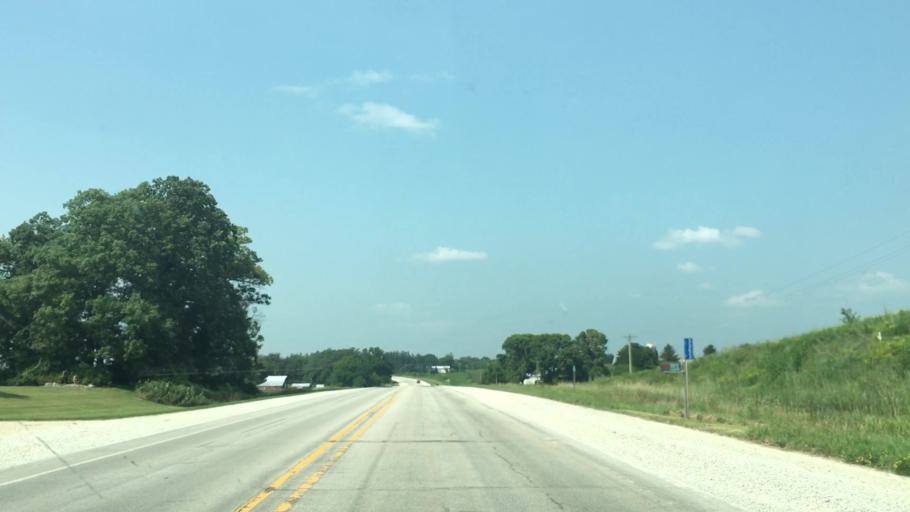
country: US
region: Iowa
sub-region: Winneshiek County
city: Decorah
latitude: 43.4219
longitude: -91.8593
